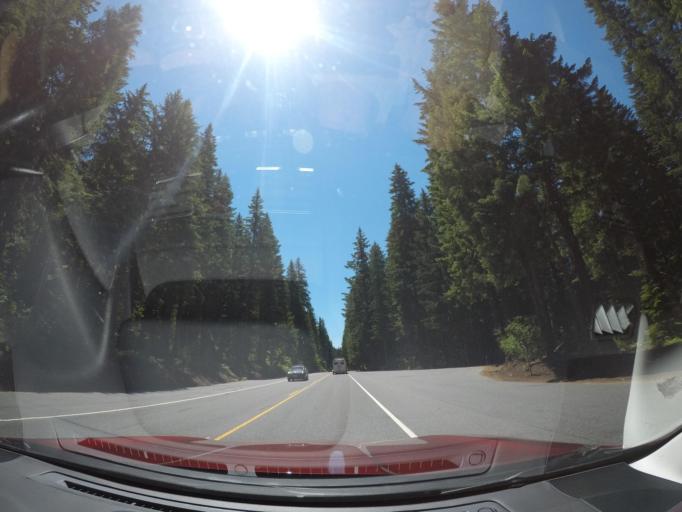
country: US
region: Oregon
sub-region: Deschutes County
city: Sisters
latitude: 44.5298
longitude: -121.9946
